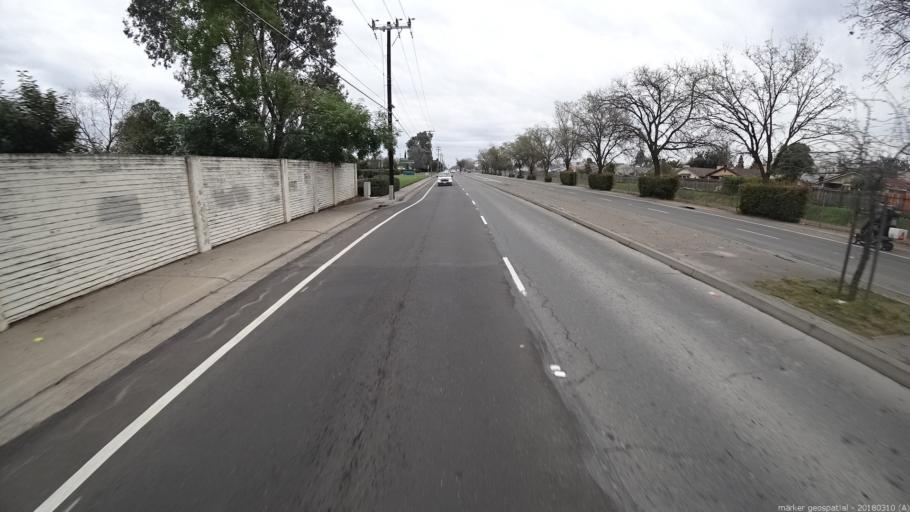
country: US
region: California
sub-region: Sacramento County
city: Florin
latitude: 38.4817
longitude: -121.4183
